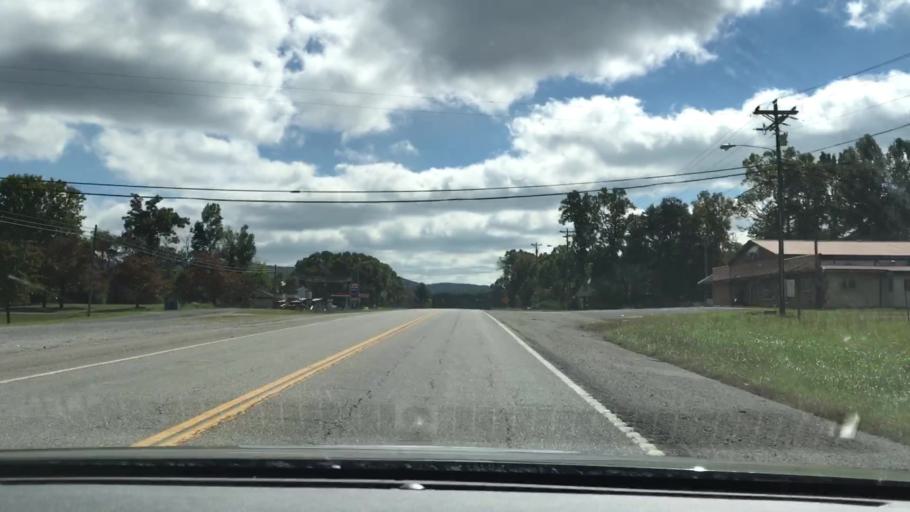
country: US
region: Tennessee
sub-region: Scott County
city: Oneida
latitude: 36.5607
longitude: -84.4499
